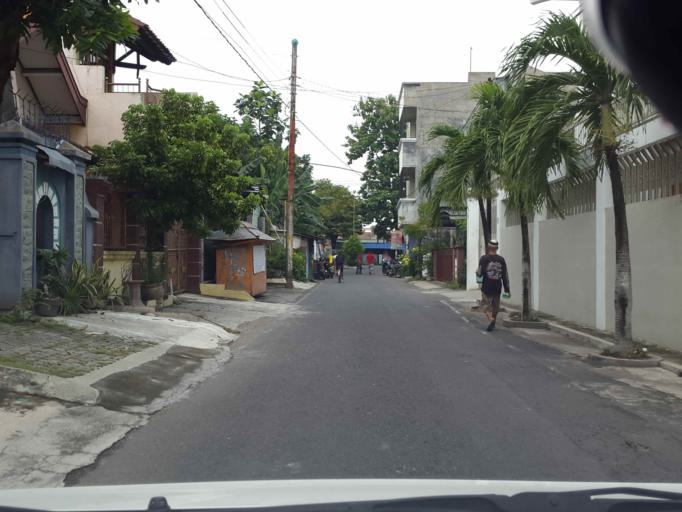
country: ID
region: Central Java
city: Grogol
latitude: -7.5784
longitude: 110.8143
